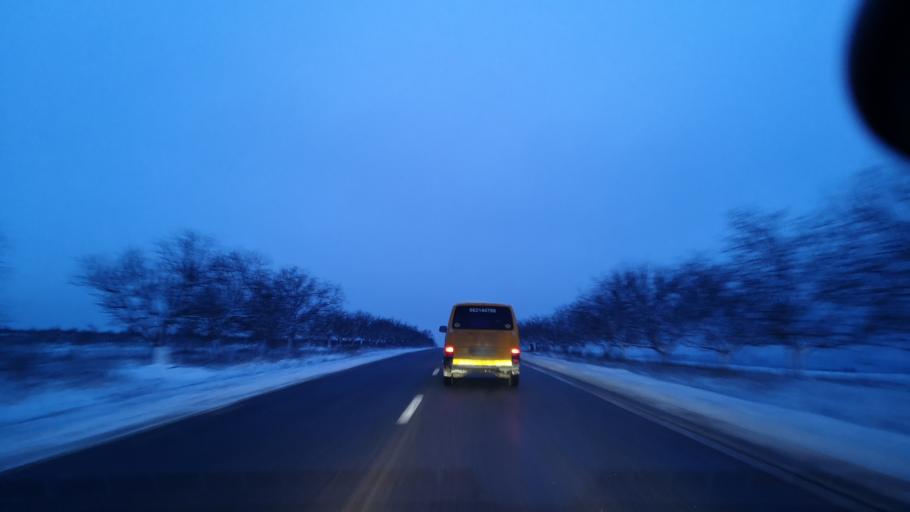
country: MD
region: Rezina
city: Saharna
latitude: 47.6188
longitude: 28.8327
